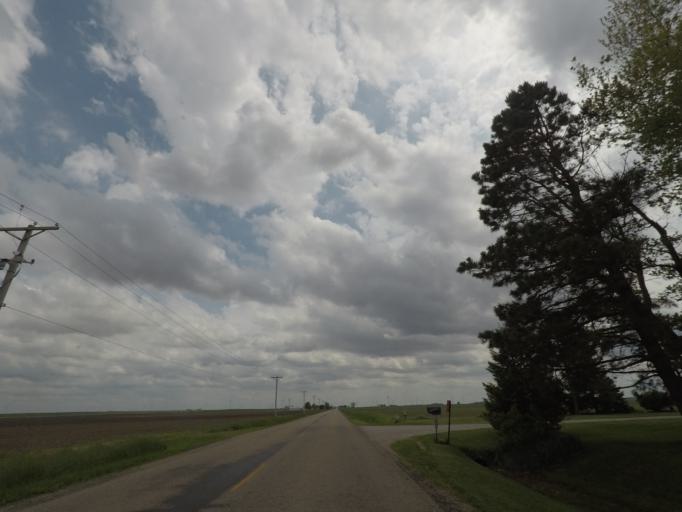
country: US
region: Illinois
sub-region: Macon County
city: Maroa
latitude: 40.0818
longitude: -89.0859
